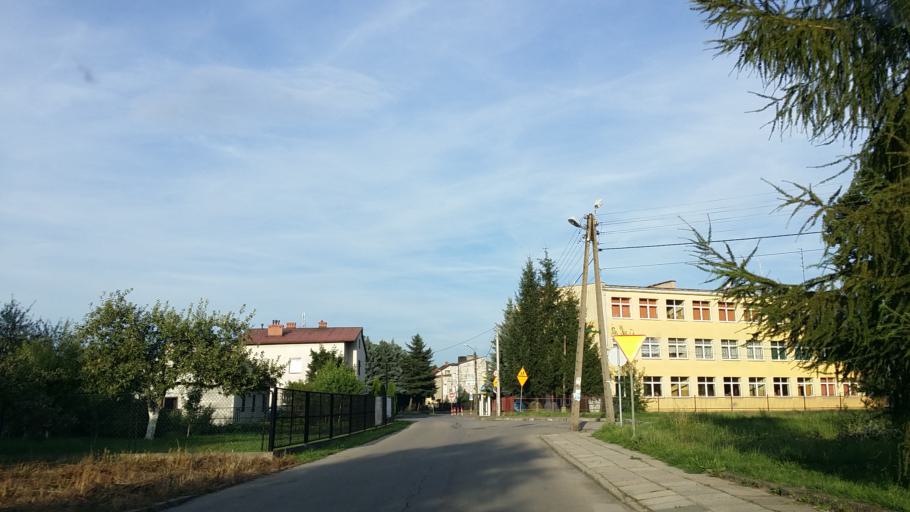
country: PL
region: Lesser Poland Voivodeship
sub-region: Powiat oswiecimski
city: Zator
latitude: 49.9946
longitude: 19.4341
